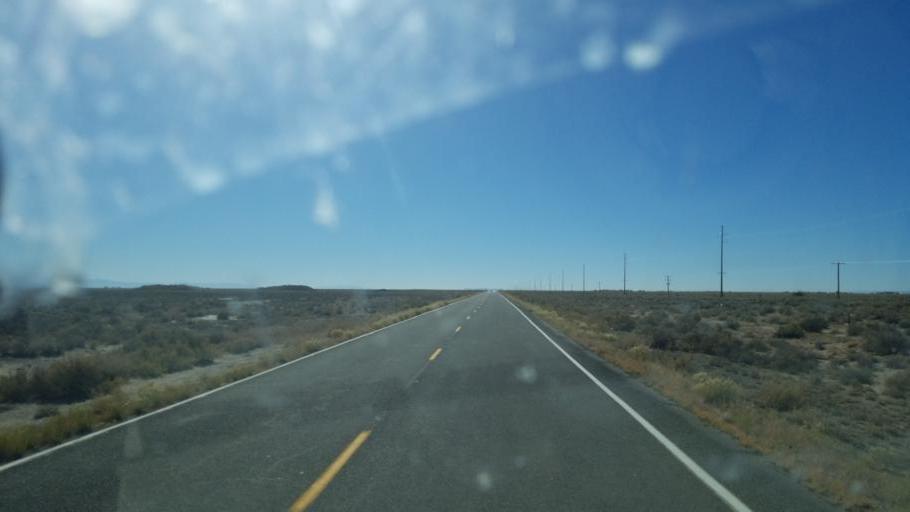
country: US
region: Colorado
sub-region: Saguache County
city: Center
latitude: 37.8806
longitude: -105.8952
